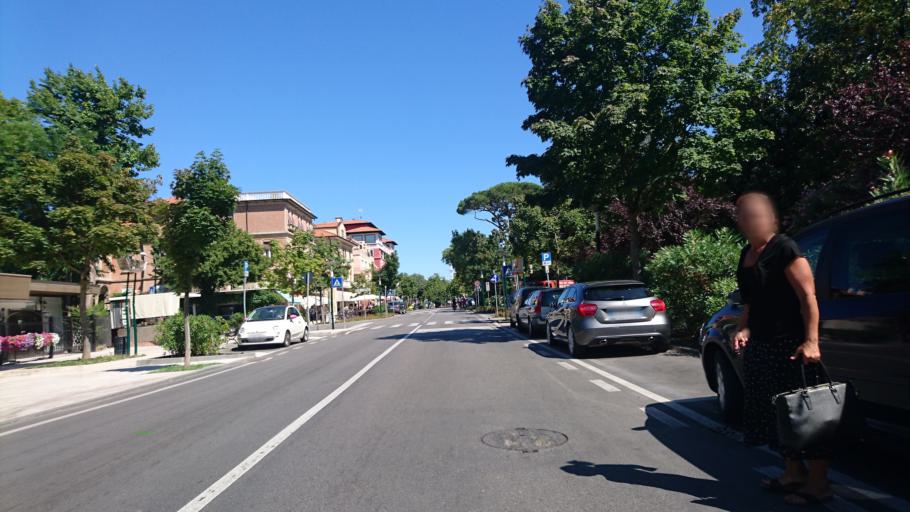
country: IT
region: Veneto
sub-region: Provincia di Venezia
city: Lido
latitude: 45.4156
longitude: 12.3731
